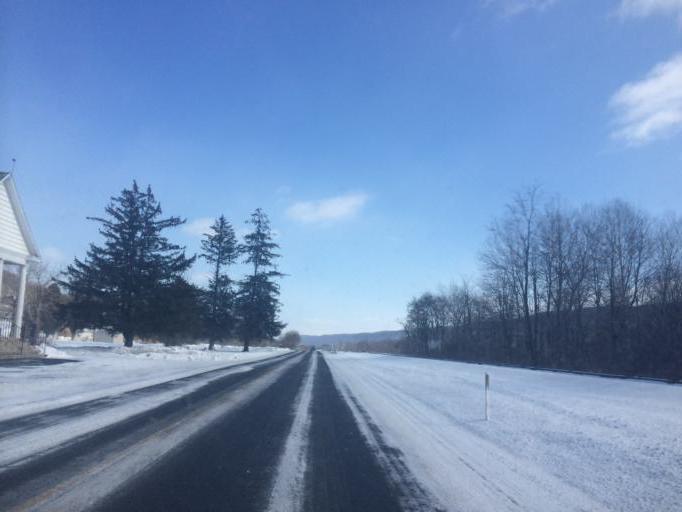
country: US
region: Pennsylvania
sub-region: Centre County
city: Stormstown
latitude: 40.8384
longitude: -77.9978
